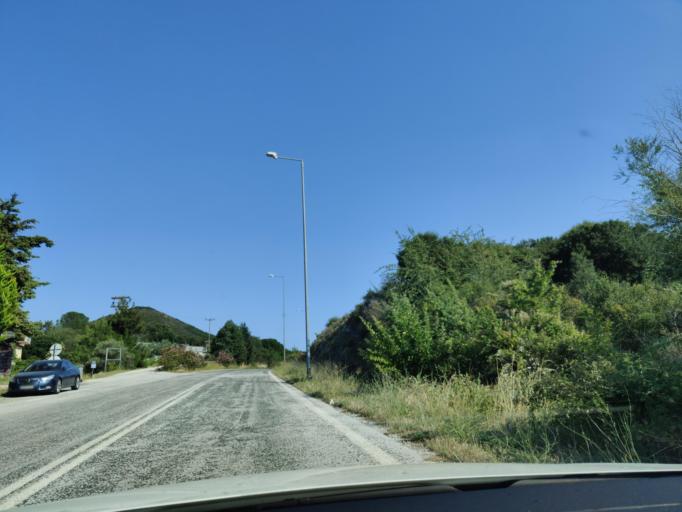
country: GR
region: East Macedonia and Thrace
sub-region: Nomos Kavalas
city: Nea Iraklitsa
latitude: 40.8650
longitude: 24.2996
